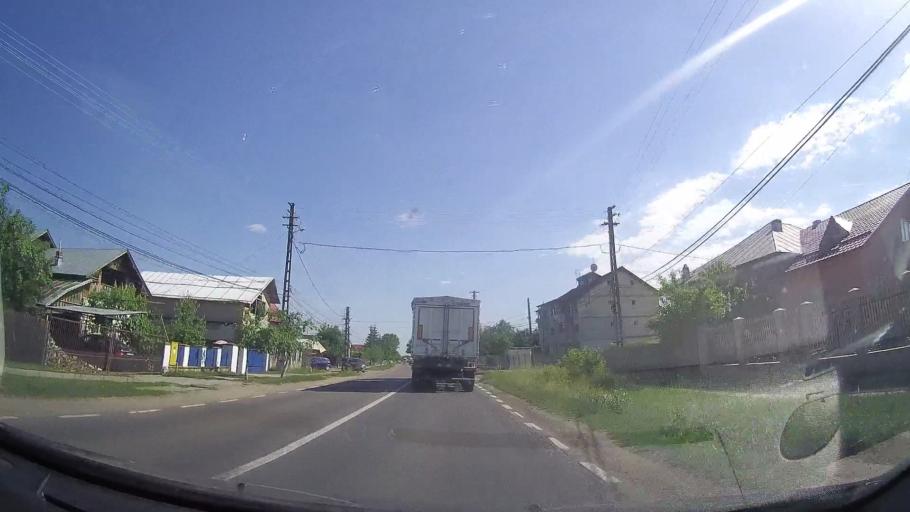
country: RO
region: Prahova
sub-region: Comuna Gura Vitioarei
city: Gura Vitioarei
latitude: 45.1516
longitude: 26.0288
